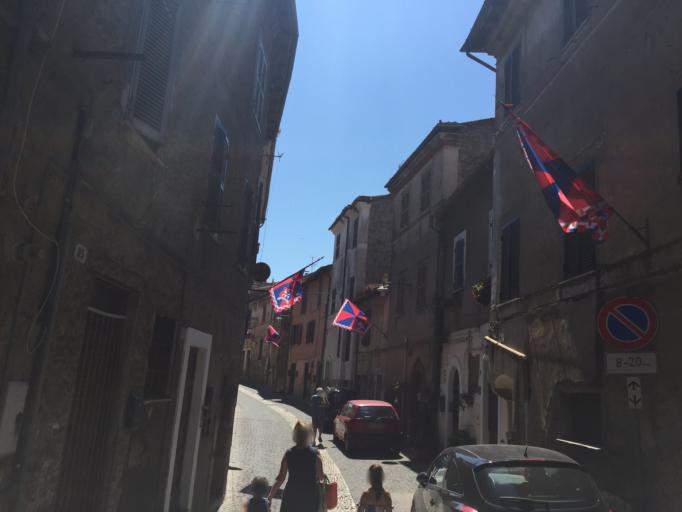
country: IT
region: Latium
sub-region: Provincia di Latina
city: Cori
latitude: 41.6408
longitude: 12.9137
